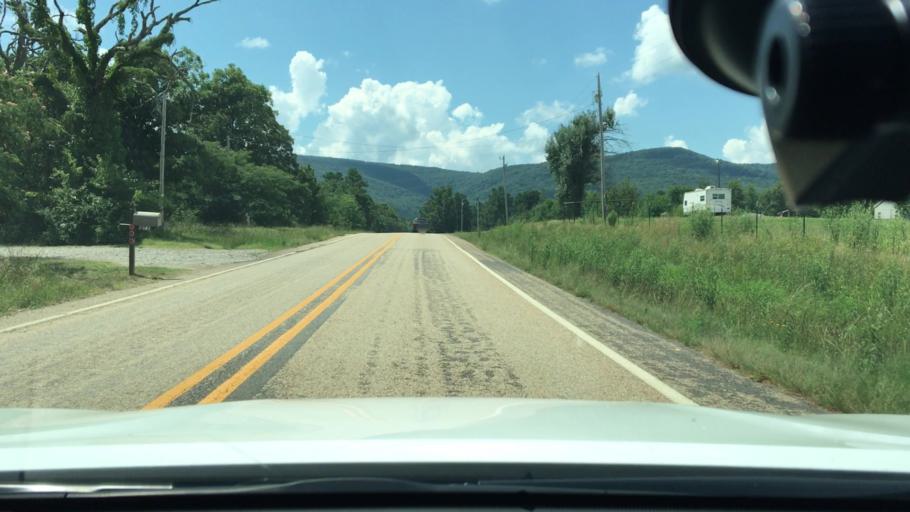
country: US
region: Arkansas
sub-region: Logan County
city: Paris
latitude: 35.2044
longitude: -93.6347
